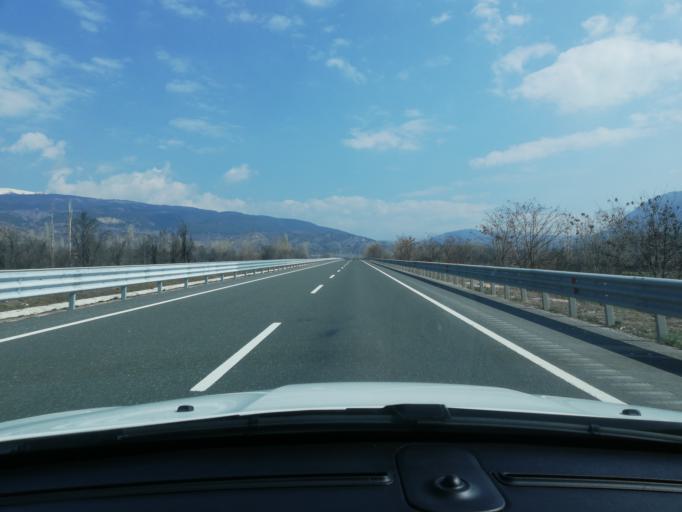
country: TR
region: Cankiri
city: Ilgaz
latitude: 40.9422
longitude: 33.6592
